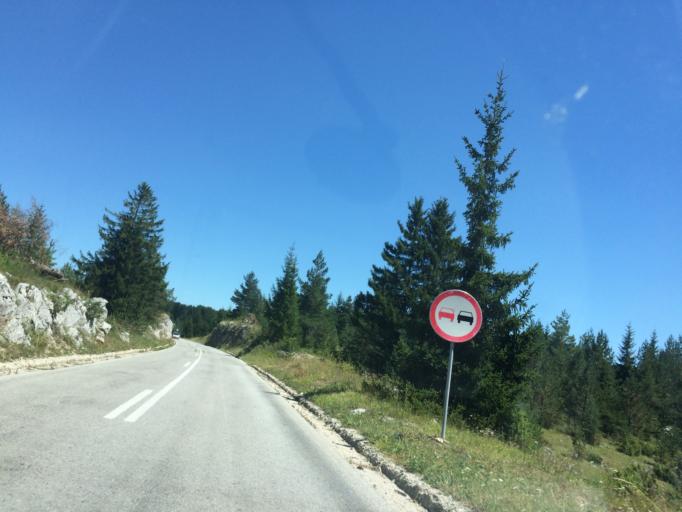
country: ME
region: Pljevlja
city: Pljevlja
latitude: 43.3405
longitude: 19.4856
